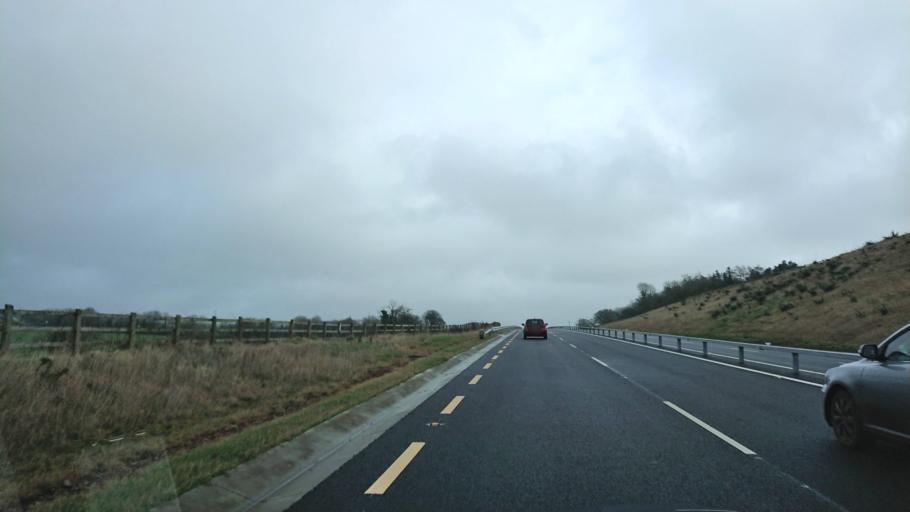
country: IE
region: Leinster
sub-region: Loch Garman
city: New Ross
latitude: 52.3718
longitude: -6.9298
